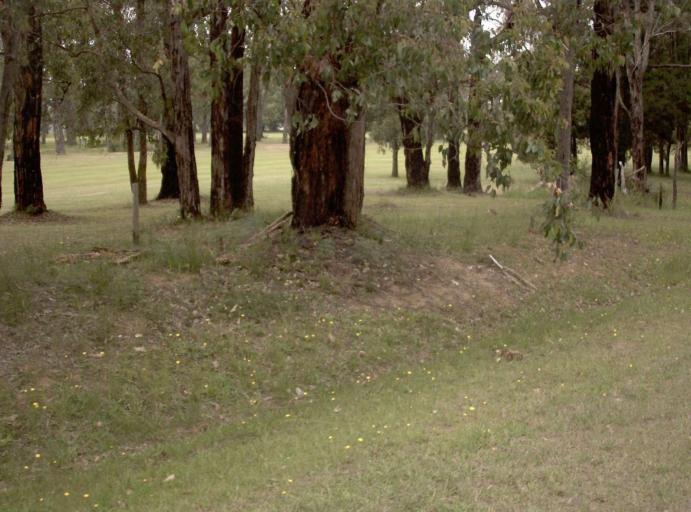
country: AU
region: Victoria
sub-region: Latrobe
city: Moe
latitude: -38.3962
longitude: 146.1650
